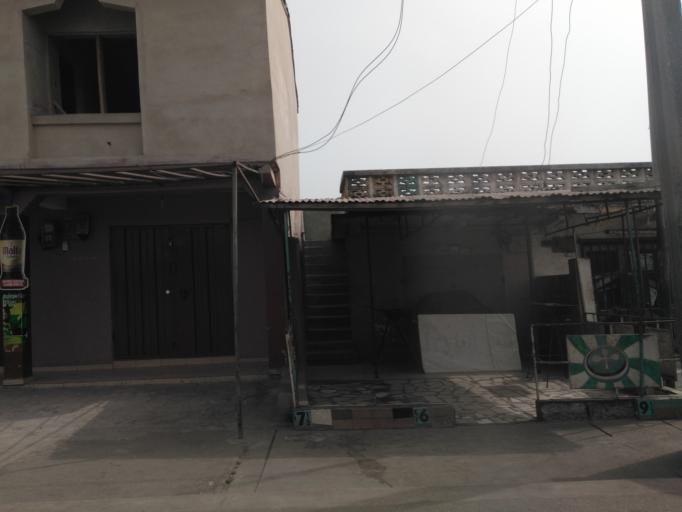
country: GH
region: Ashanti
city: Kumasi
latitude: 6.7039
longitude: -1.6078
